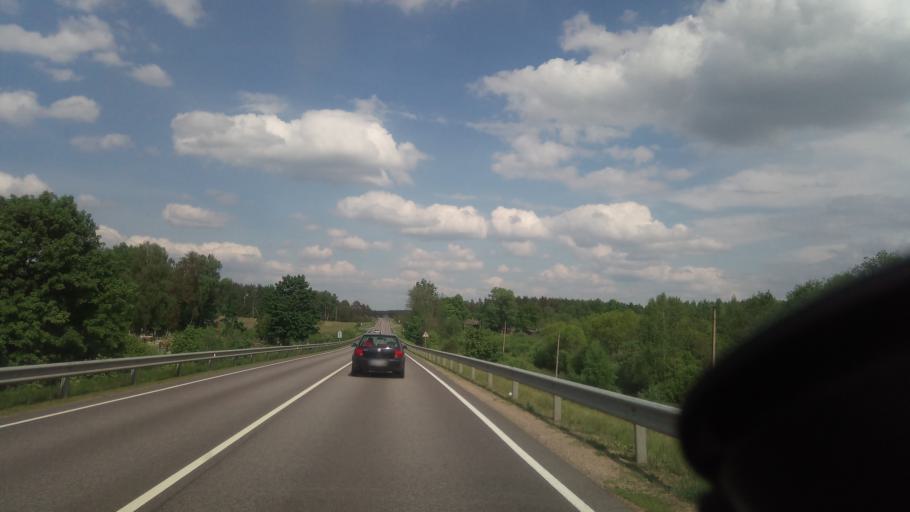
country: LT
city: Trakai
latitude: 54.6102
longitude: 24.8739
